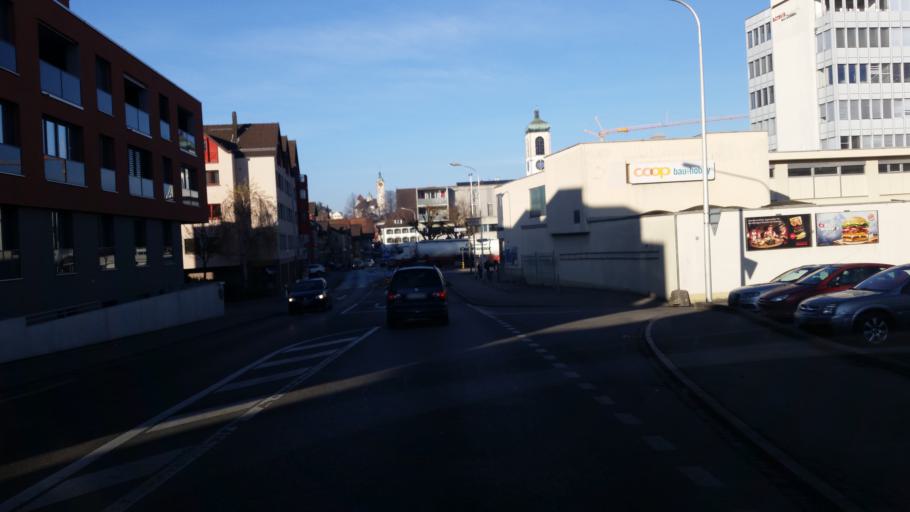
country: CH
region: Saint Gallen
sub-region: Wahlkreis St. Gallen
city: Gossau
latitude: 47.4129
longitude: 9.2491
